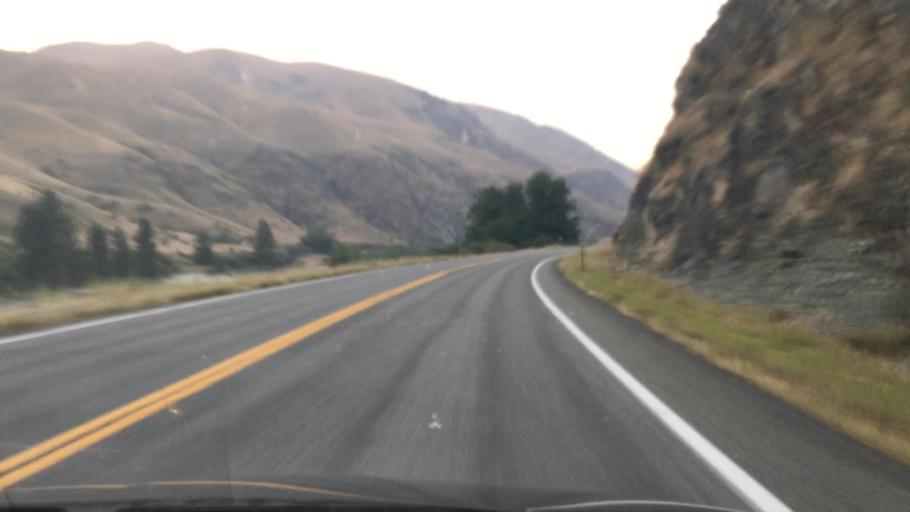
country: US
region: Idaho
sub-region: Idaho County
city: Grangeville
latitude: 45.5705
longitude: -116.3048
